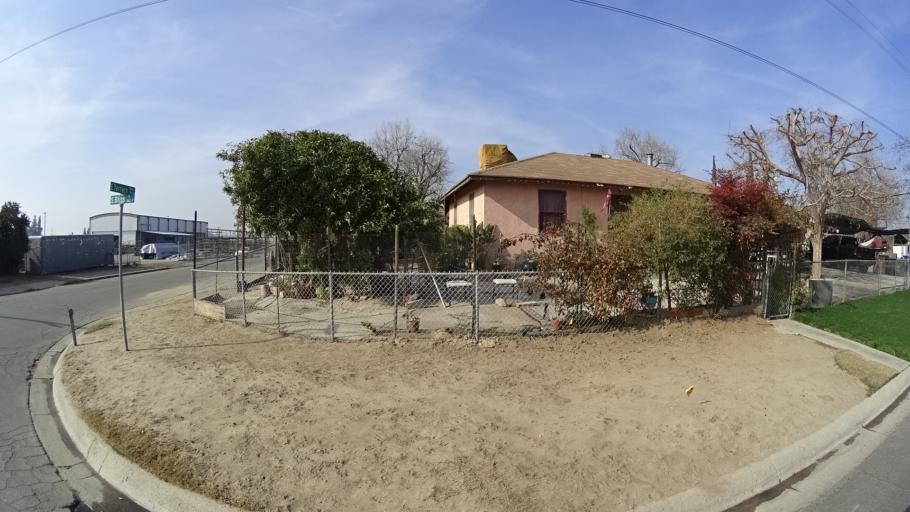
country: US
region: California
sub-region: Kern County
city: Bakersfield
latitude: 35.3504
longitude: -118.9985
